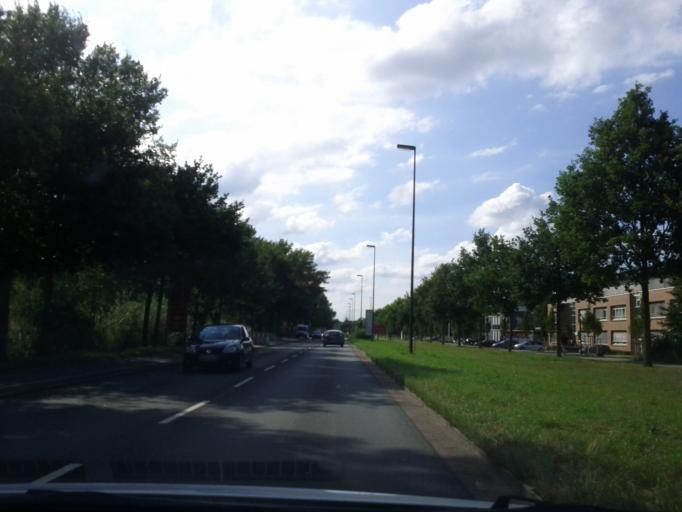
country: DE
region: Bremen
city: Bremen
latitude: 53.1115
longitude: 8.8520
